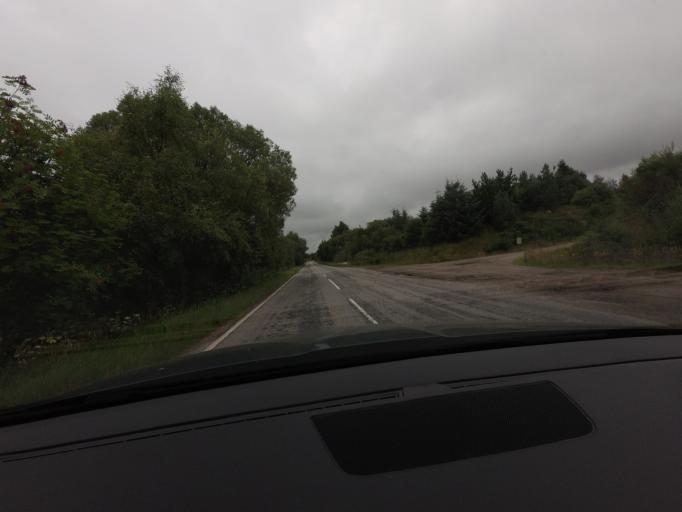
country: GB
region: Scotland
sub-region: Highland
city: Alness
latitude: 58.0401
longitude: -4.4248
